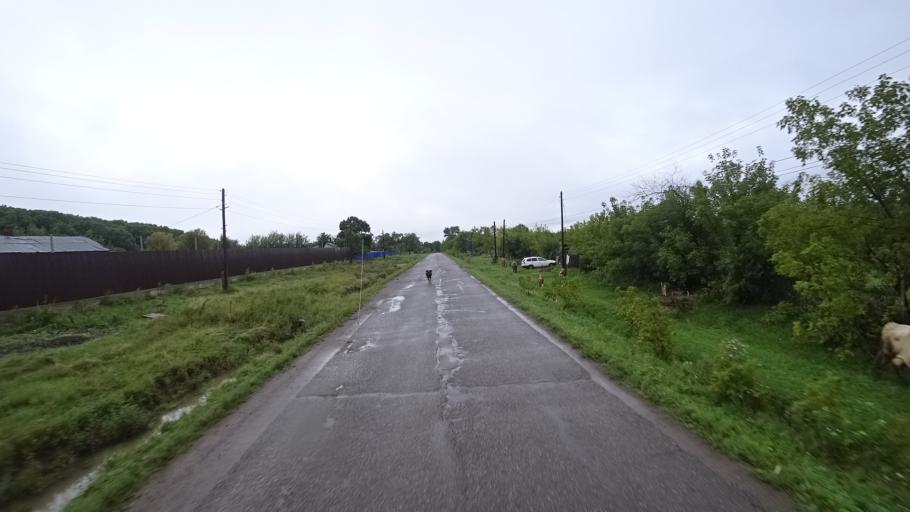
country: RU
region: Primorskiy
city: Monastyrishche
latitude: 44.2650
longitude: 132.4205
